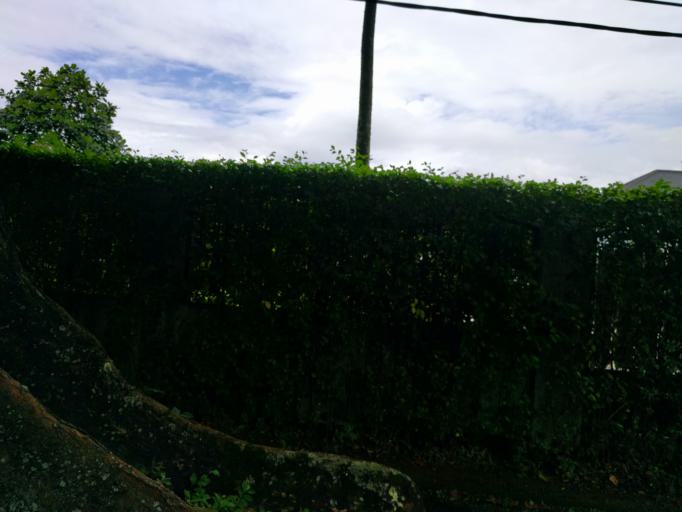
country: ID
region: West Java
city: Bogor
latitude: -6.5912
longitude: 106.8031
